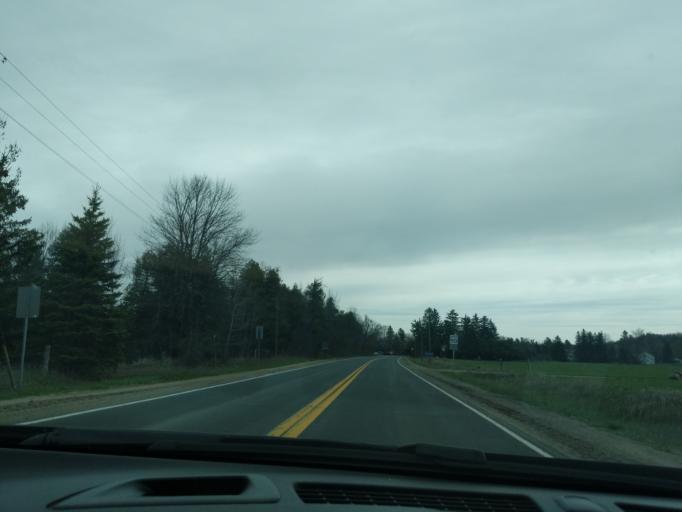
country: CA
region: Ontario
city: Orangeville
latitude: 44.0198
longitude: -79.9738
